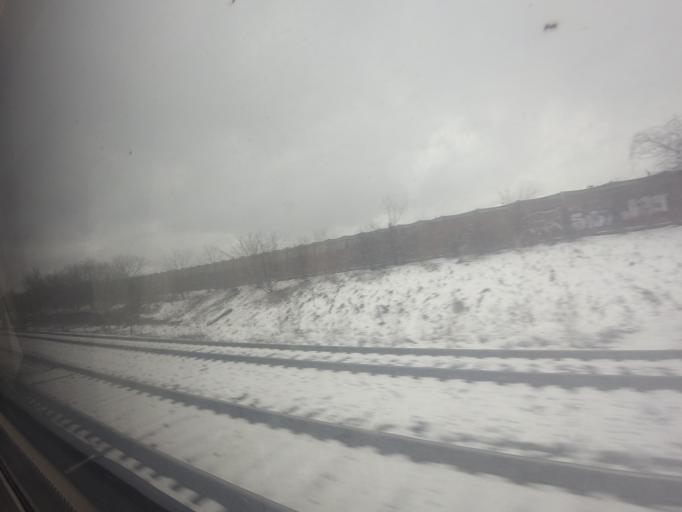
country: CA
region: Ontario
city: Scarborough
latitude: 43.7112
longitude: -79.2587
